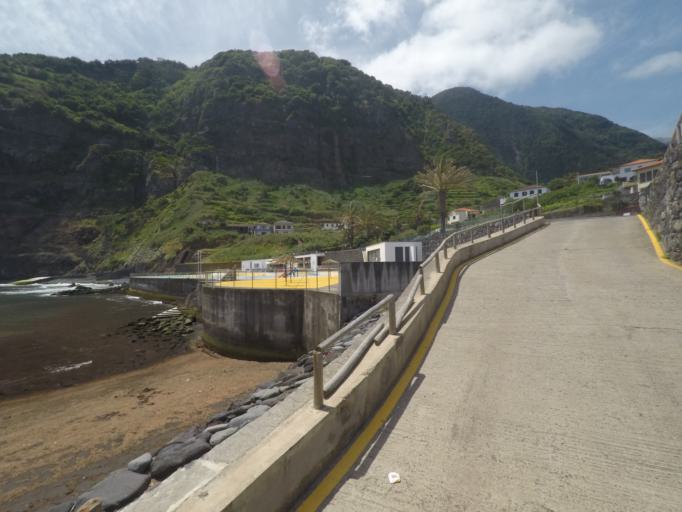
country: PT
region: Madeira
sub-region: Sao Vicente
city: Sao Vicente
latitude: 32.8285
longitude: -16.9850
